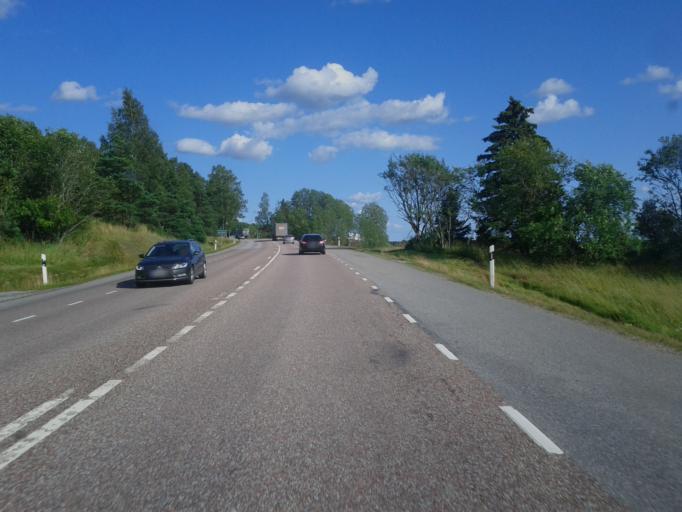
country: SE
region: Uppsala
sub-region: Enkopings Kommun
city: Irsta
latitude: 59.7037
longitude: 16.9916
